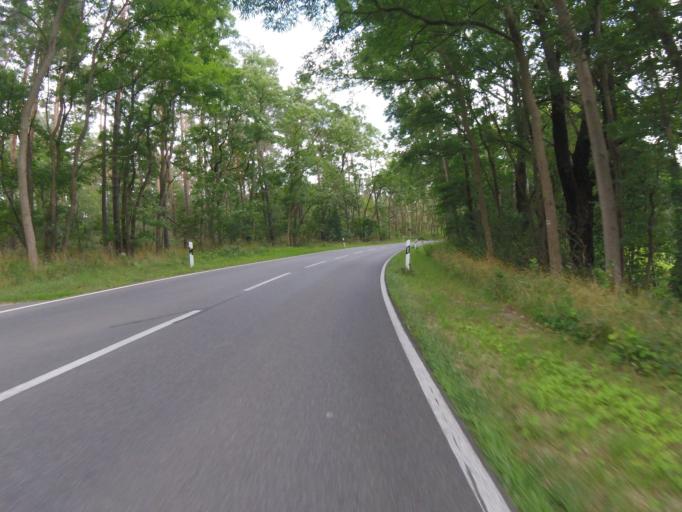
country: DE
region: Brandenburg
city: Halbe
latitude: 52.0866
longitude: 13.7301
